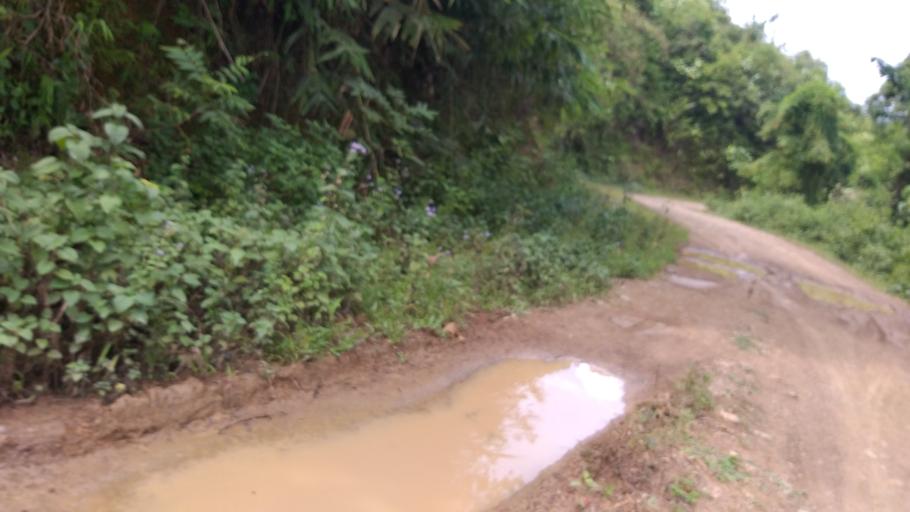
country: VN
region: Huyen Dien Bien
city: Dien Bien Phu
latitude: 21.4689
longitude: 102.6821
